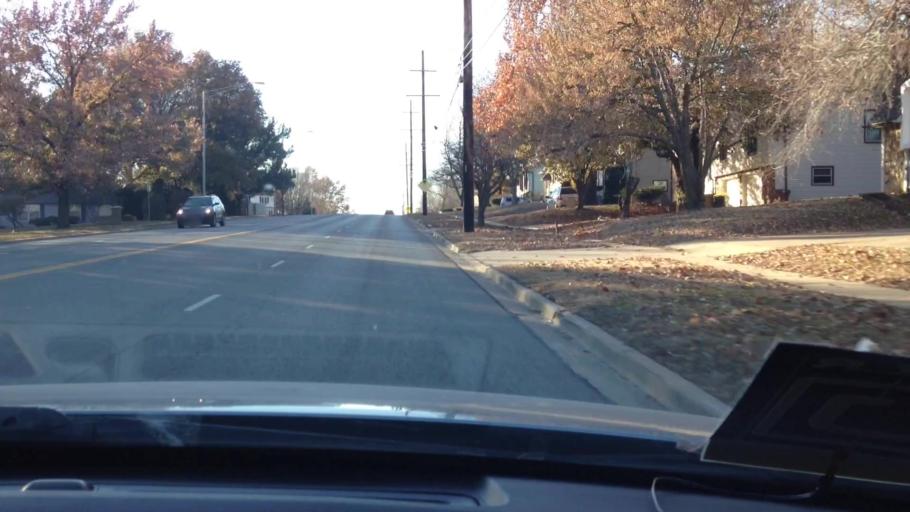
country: US
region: Kansas
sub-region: Johnson County
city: Overland Park
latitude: 38.9568
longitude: -94.6542
